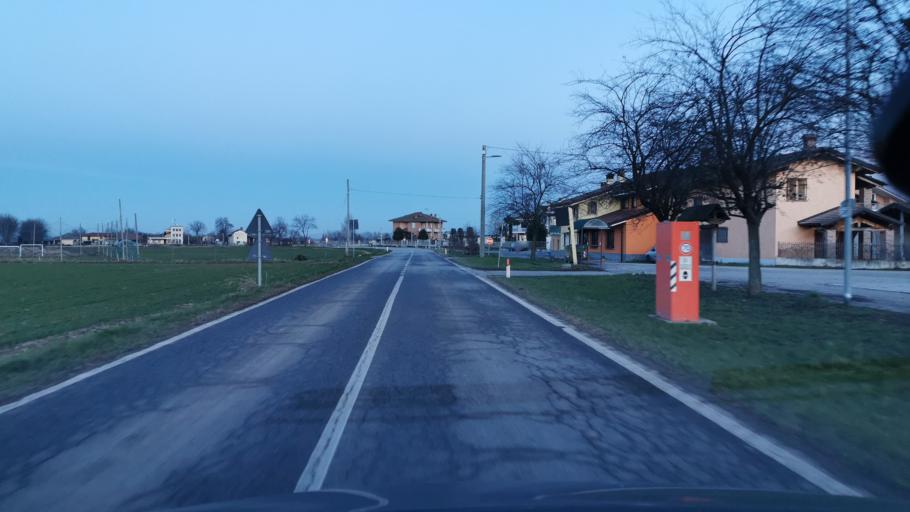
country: IT
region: Piedmont
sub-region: Provincia di Cuneo
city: Caraglio
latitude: 44.4313
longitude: 7.4494
